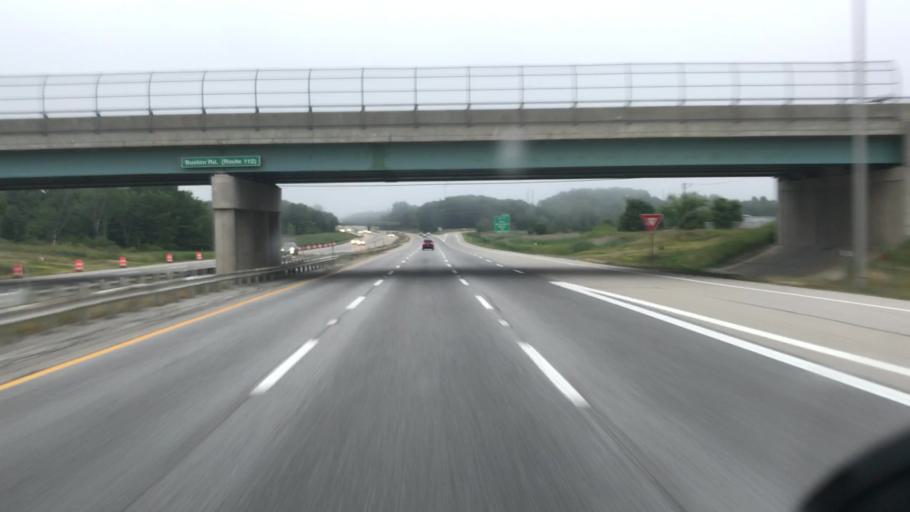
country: US
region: Maine
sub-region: York County
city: Saco
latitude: 43.5222
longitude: -70.4595
